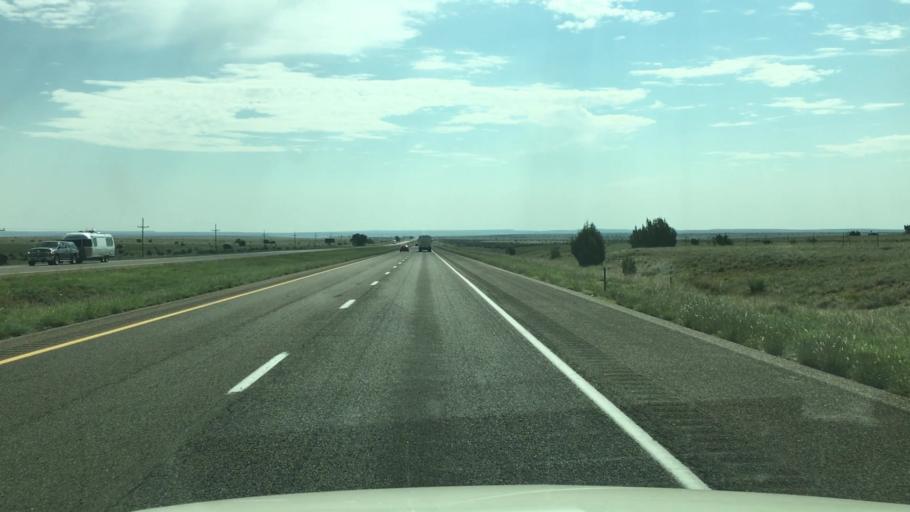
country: US
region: New Mexico
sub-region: Guadalupe County
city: Santa Rosa
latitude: 34.9839
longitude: -105.1423
